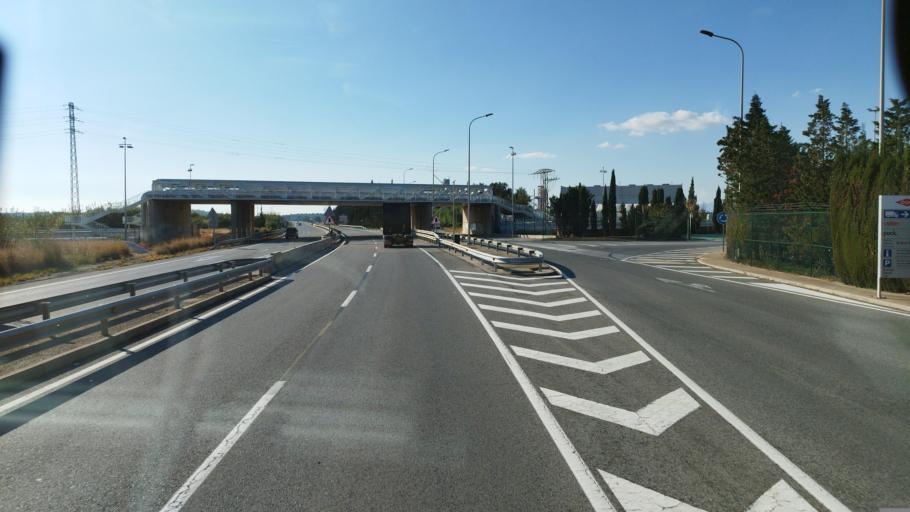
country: ES
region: Catalonia
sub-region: Provincia de Barcelona
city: La Pineda
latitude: 41.1008
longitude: 1.1873
